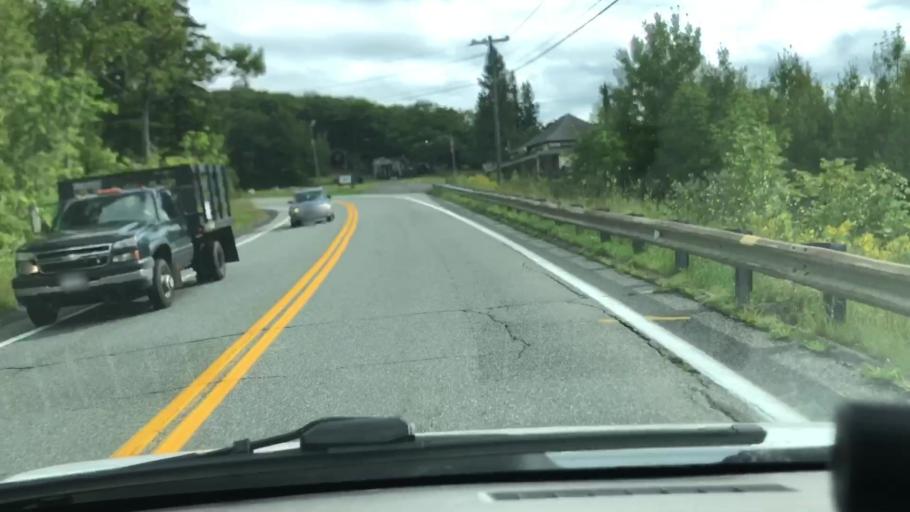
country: US
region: Massachusetts
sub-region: Berkshire County
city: North Adams
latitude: 42.6980
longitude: -73.0658
